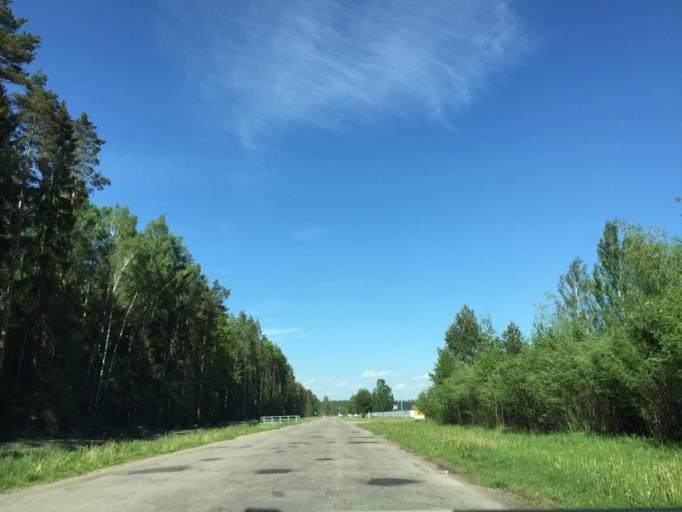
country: LV
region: Ozolnieku
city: Ozolnieki
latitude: 56.6633
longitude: 23.7919
